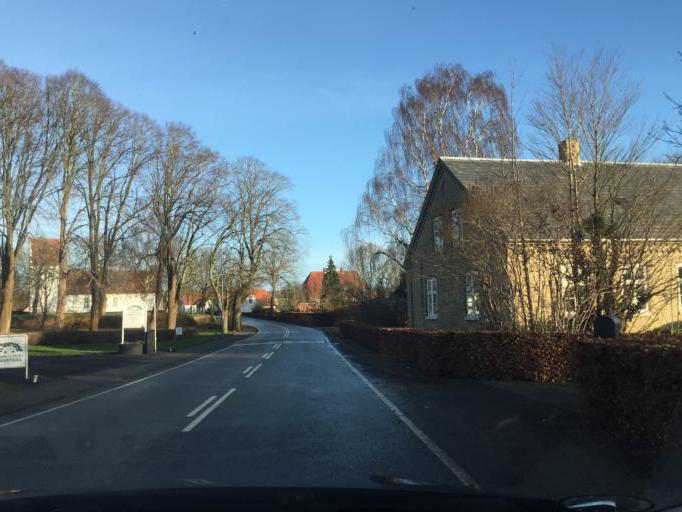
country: DK
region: South Denmark
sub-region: Middelfart Kommune
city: Ejby
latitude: 55.4354
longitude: 9.9409
